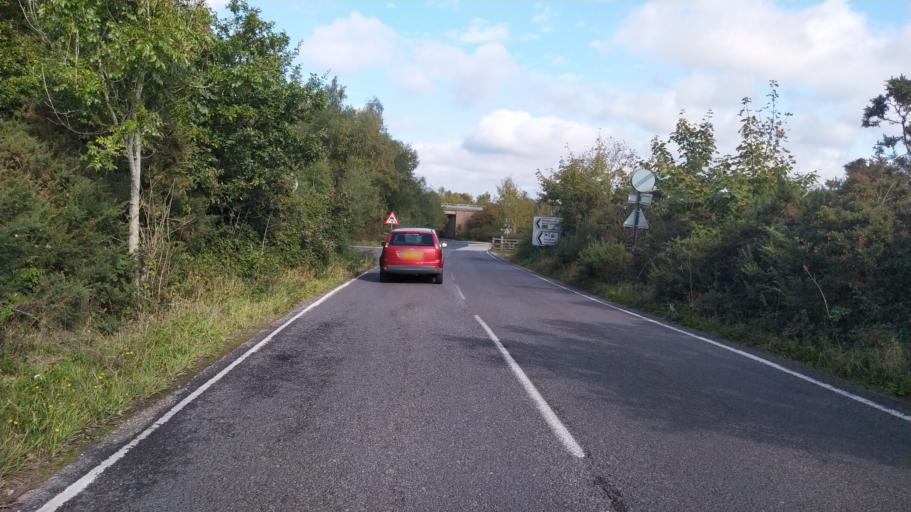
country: GB
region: England
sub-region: Hampshire
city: Ringwood
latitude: 50.8532
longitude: -1.7289
